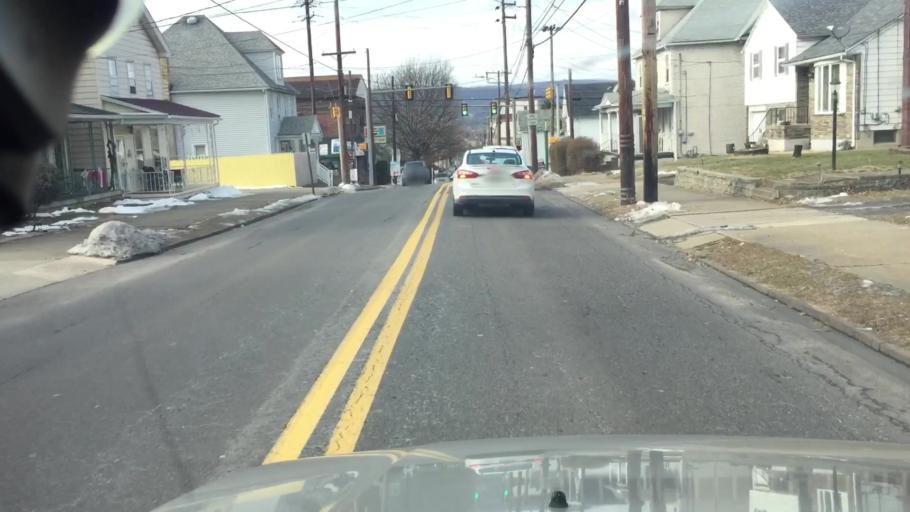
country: US
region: Pennsylvania
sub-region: Luzerne County
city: Ashley
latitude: 41.2301
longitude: -75.8992
